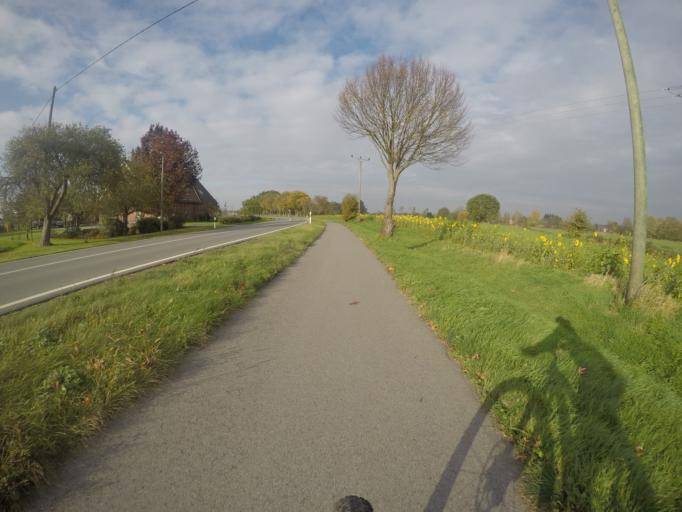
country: DE
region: North Rhine-Westphalia
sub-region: Regierungsbezirk Munster
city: Isselburg
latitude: 51.8382
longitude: 6.4807
